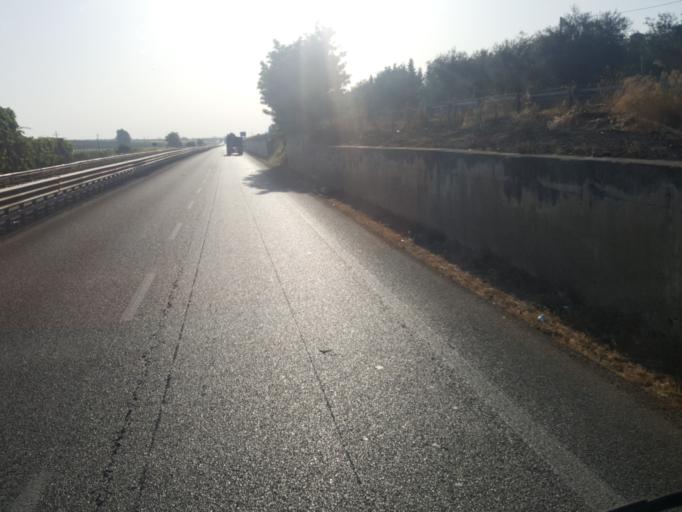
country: IT
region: Apulia
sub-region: Provincia di Barletta - Andria - Trani
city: San Ferdinando di Puglia
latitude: 41.2851
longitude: 16.0073
